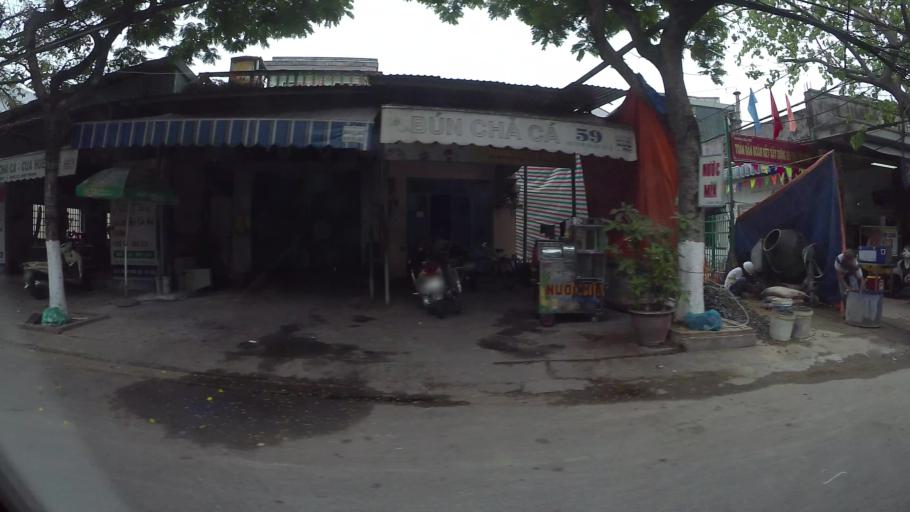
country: VN
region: Da Nang
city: Thanh Khe
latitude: 16.0633
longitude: 108.1843
